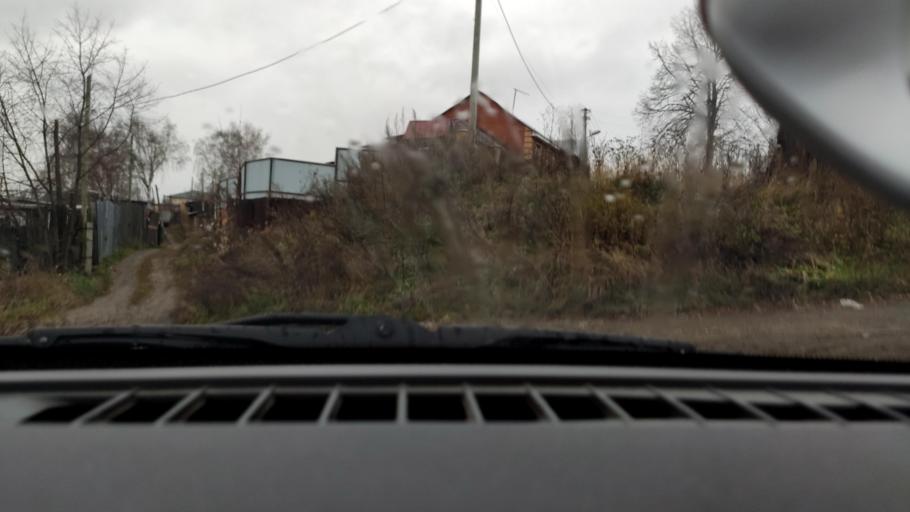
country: RU
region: Perm
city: Kondratovo
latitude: 57.9591
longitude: 56.1660
